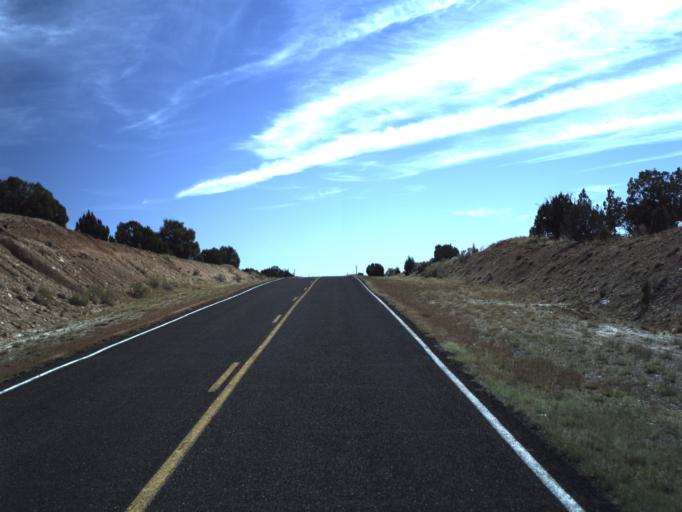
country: US
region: Utah
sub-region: Wayne County
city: Loa
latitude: 37.7397
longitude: -111.5520
